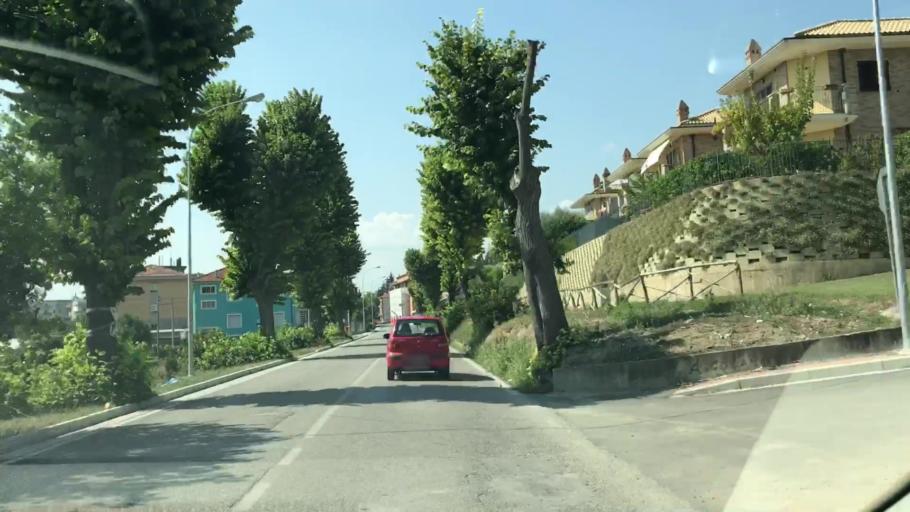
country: IT
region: The Marches
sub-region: Provincia di Ascoli Piceno
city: Stella
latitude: 42.8891
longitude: 13.8224
